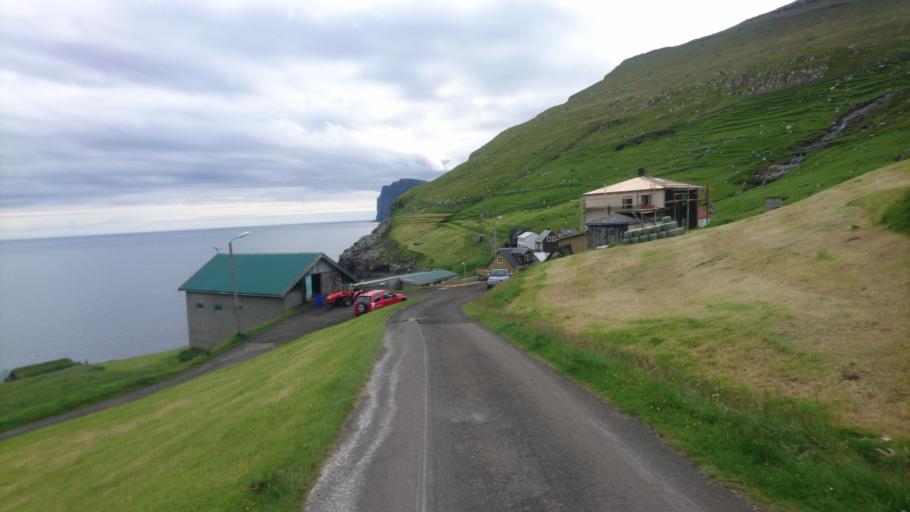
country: FO
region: Nordoyar
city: Klaksvik
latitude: 62.3301
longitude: -6.2756
